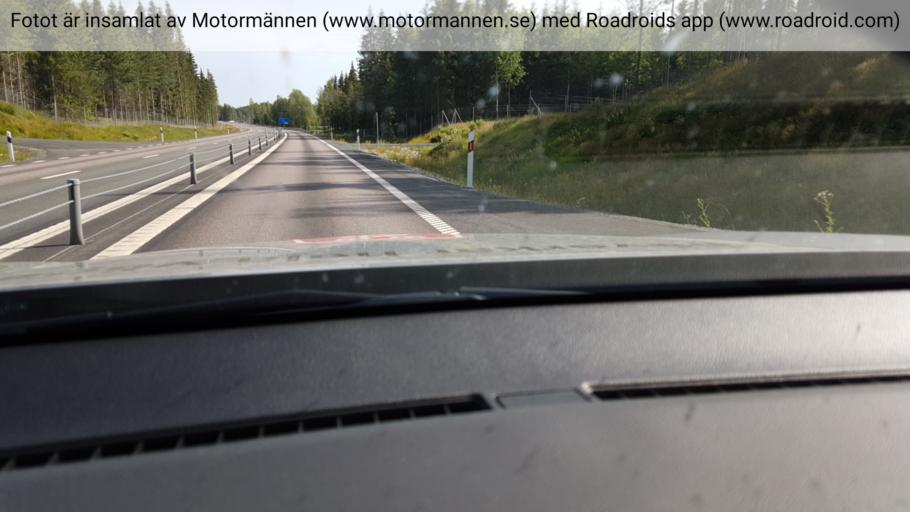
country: SE
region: Joenkoeping
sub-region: Aneby Kommun
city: Aneby
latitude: 57.8544
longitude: 14.8648
